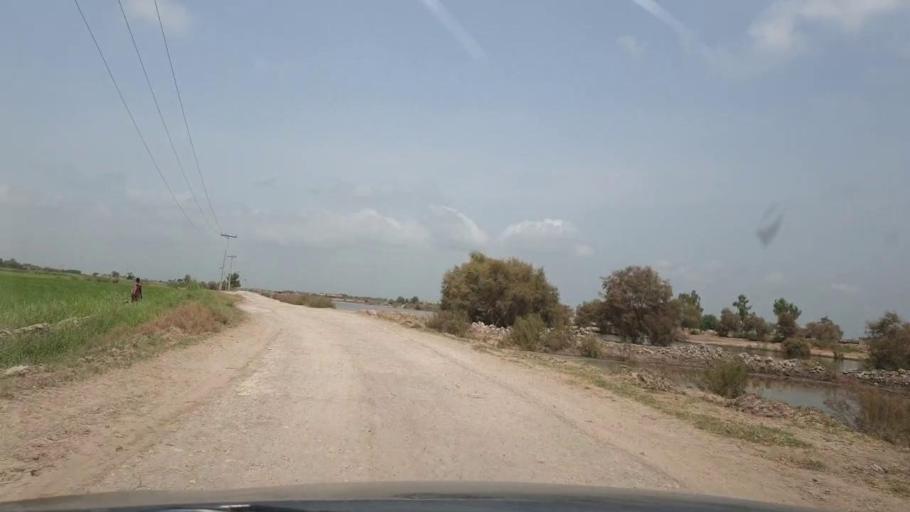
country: PK
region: Sindh
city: Ratodero
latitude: 27.9057
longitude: 68.3131
